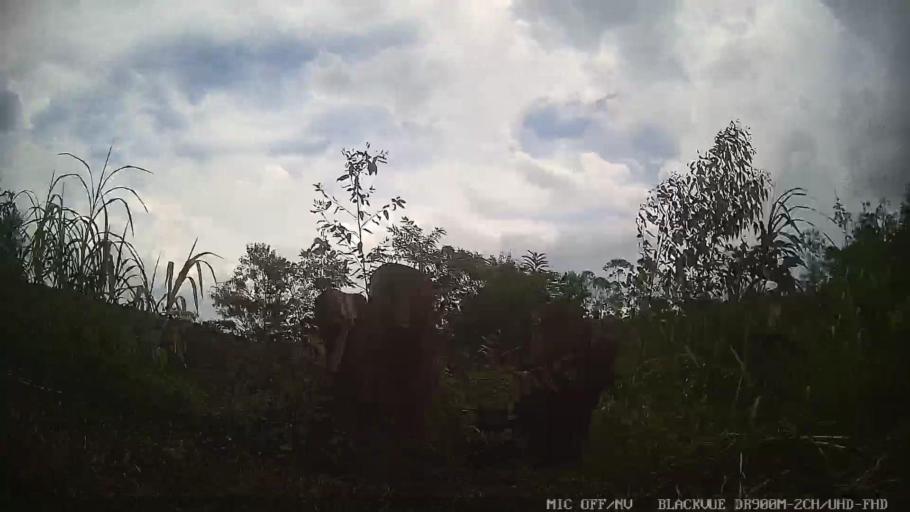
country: BR
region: Sao Paulo
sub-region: Mogi das Cruzes
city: Mogi das Cruzes
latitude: -23.4589
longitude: -46.2246
